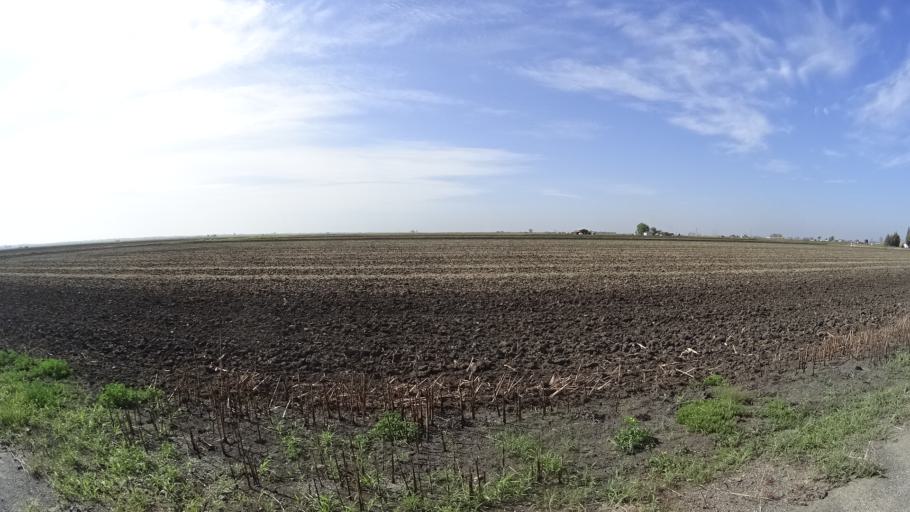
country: US
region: California
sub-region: Glenn County
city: Willows
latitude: 39.5723
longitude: -122.0432
